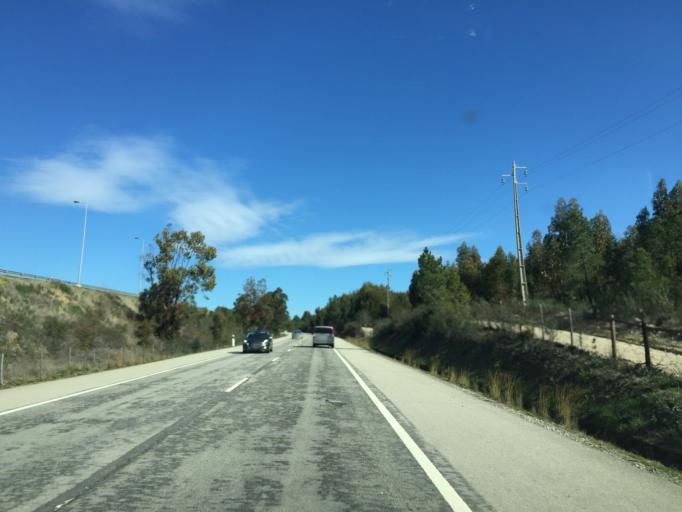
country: PT
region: Castelo Branco
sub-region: Castelo Branco
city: Castelo Branco
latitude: 39.7616
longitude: -7.6011
